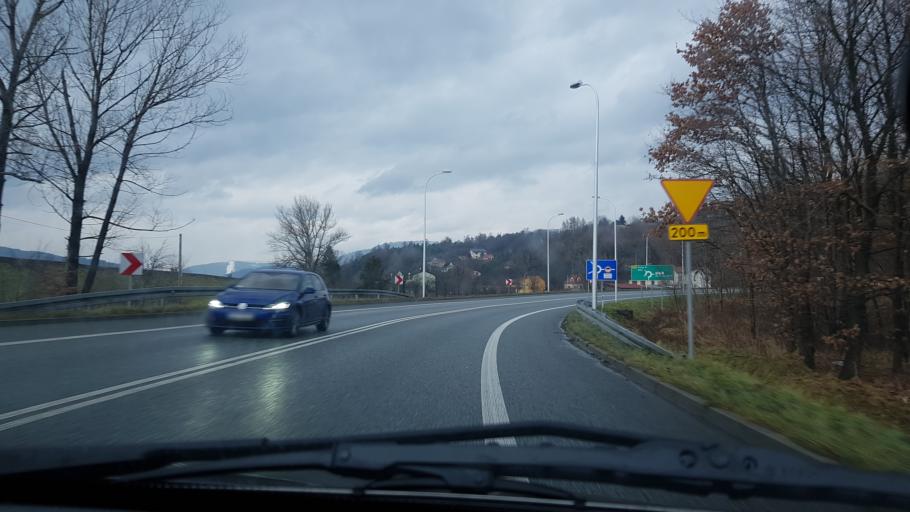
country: PL
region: Silesian Voivodeship
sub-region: Powiat zywiecki
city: Zywiec
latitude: 49.6992
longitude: 19.1989
